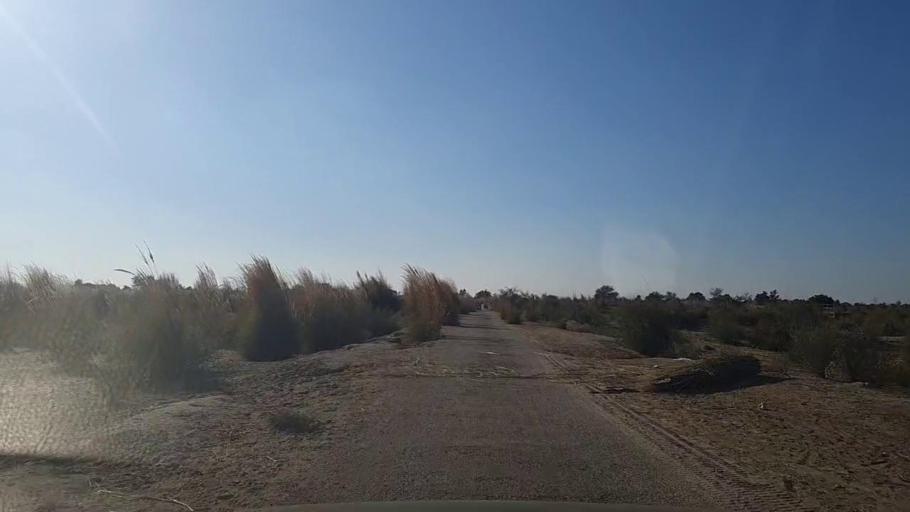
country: PK
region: Sindh
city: Khadro
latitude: 26.2413
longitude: 68.8809
